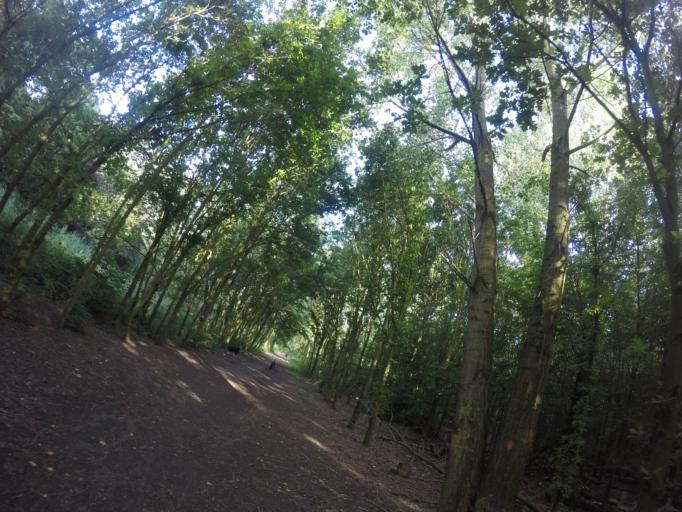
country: NL
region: Gelderland
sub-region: Gemeente Duiven
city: Duiven
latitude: 51.9470
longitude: 5.9921
